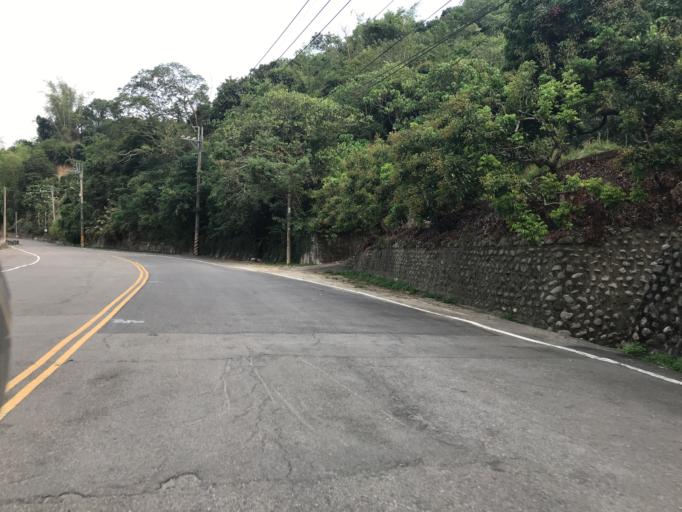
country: TW
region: Taiwan
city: Zhongxing New Village
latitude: 24.0395
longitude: 120.7080
